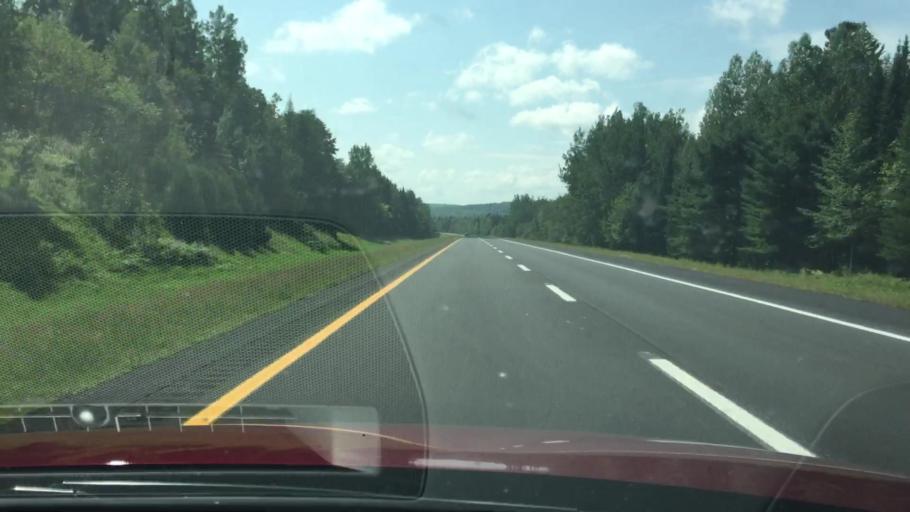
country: US
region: Maine
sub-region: Penobscot County
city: Patten
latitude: 45.8987
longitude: -68.3939
